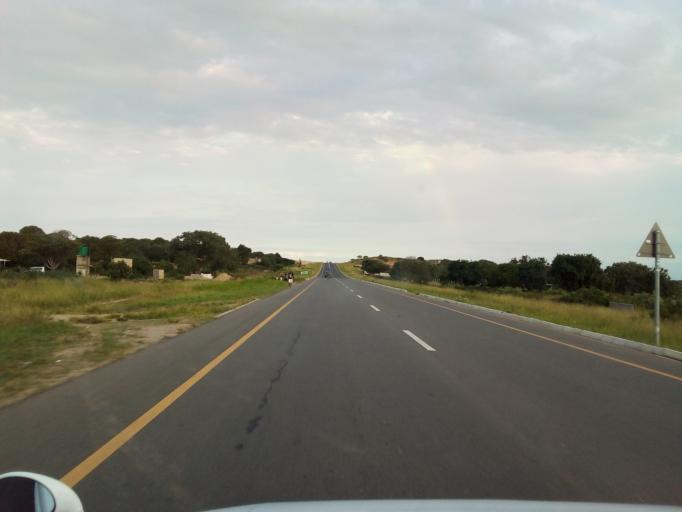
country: MZ
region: Maputo City
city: Maputo
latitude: -26.0409
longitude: 32.5634
